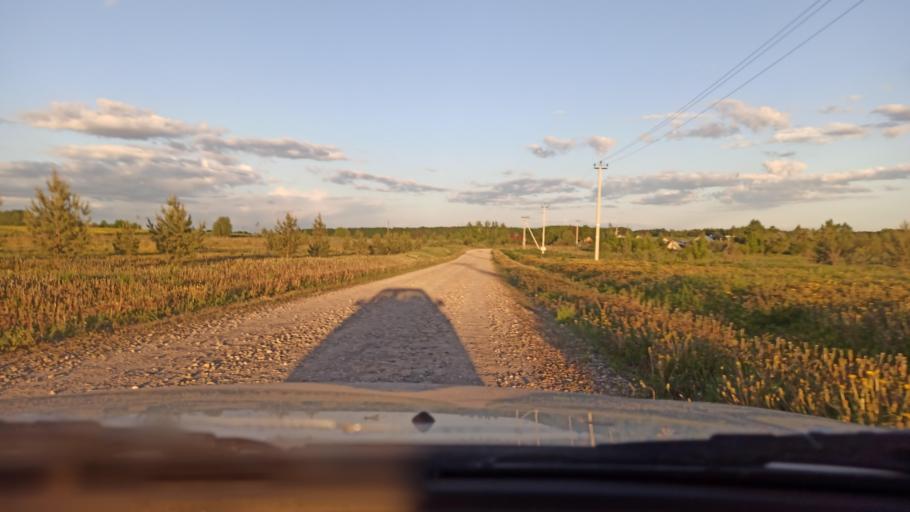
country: RU
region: Vologda
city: Molochnoye
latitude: 59.3735
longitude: 39.6926
